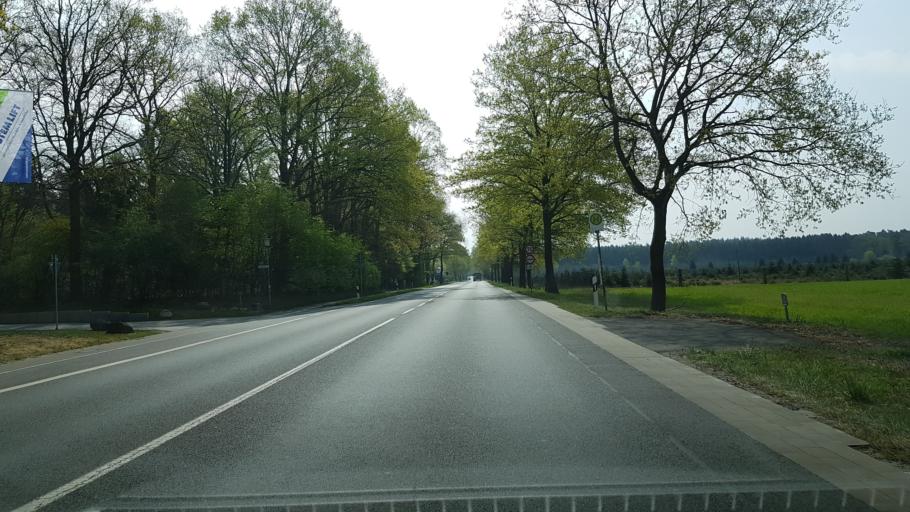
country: DE
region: Lower Saxony
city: Soltau
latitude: 52.9665
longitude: 9.8543
